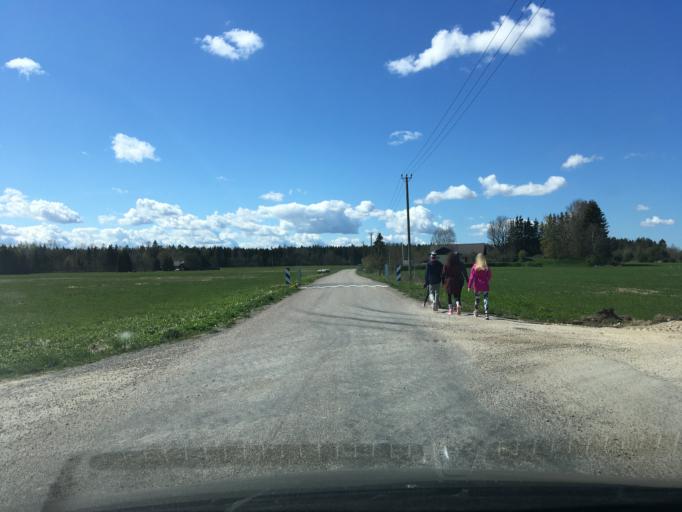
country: EE
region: Harju
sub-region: Rae vald
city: Vaida
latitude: 59.2018
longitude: 25.0910
